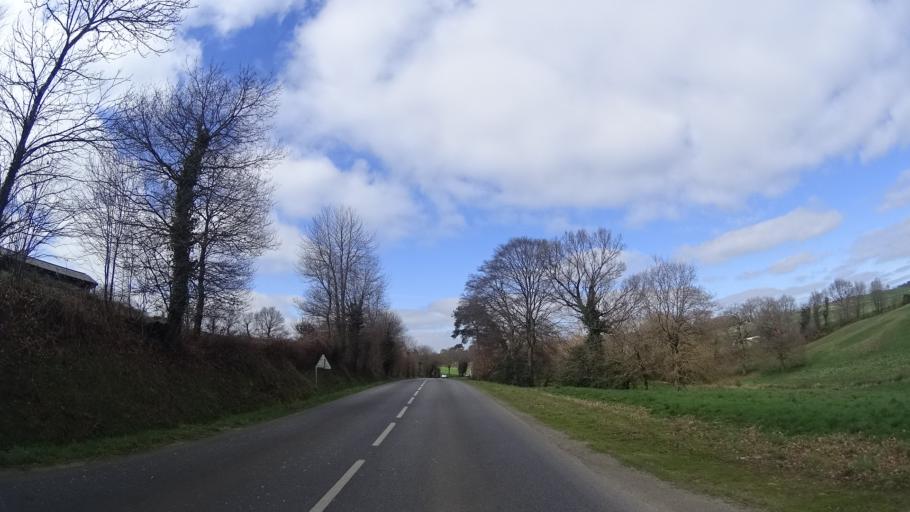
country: FR
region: Brittany
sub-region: Departement du Morbihan
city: Caro
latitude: 47.8399
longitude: -2.3138
